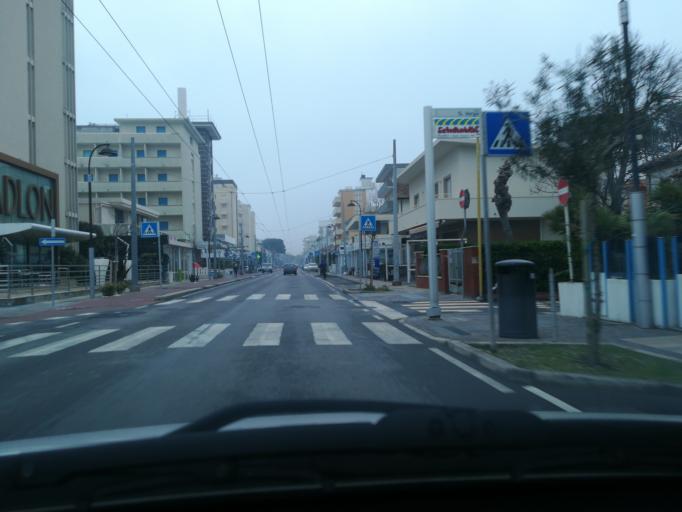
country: IT
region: Emilia-Romagna
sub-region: Provincia di Rimini
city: Riccione
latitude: 44.0149
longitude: 12.6435
